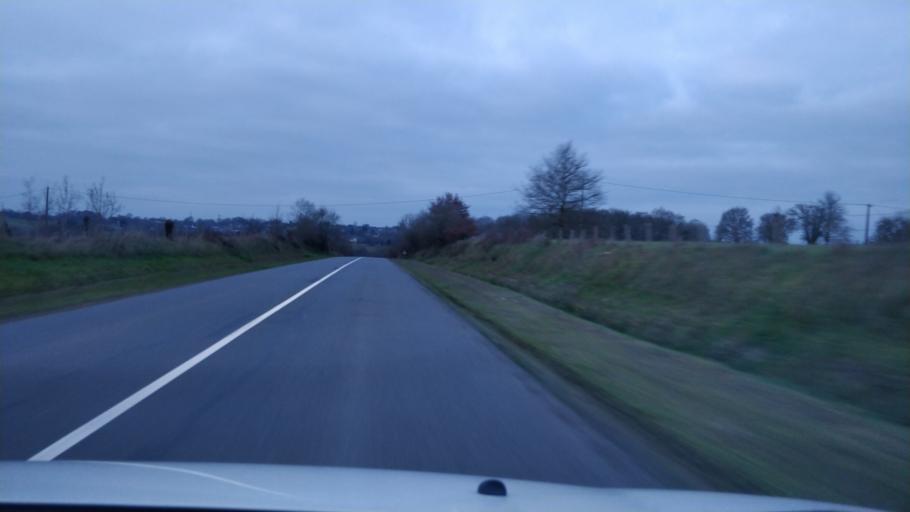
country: FR
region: Brittany
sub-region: Departement d'Ille-et-Vilaine
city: Livre-sur-Changeon
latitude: 48.2050
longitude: -1.3346
